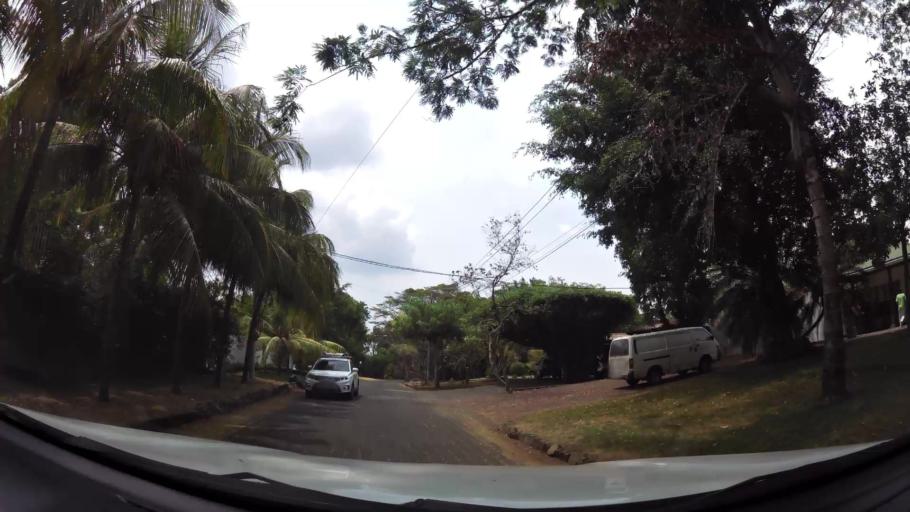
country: NI
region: Managua
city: Managua
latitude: 12.0973
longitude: -86.2347
